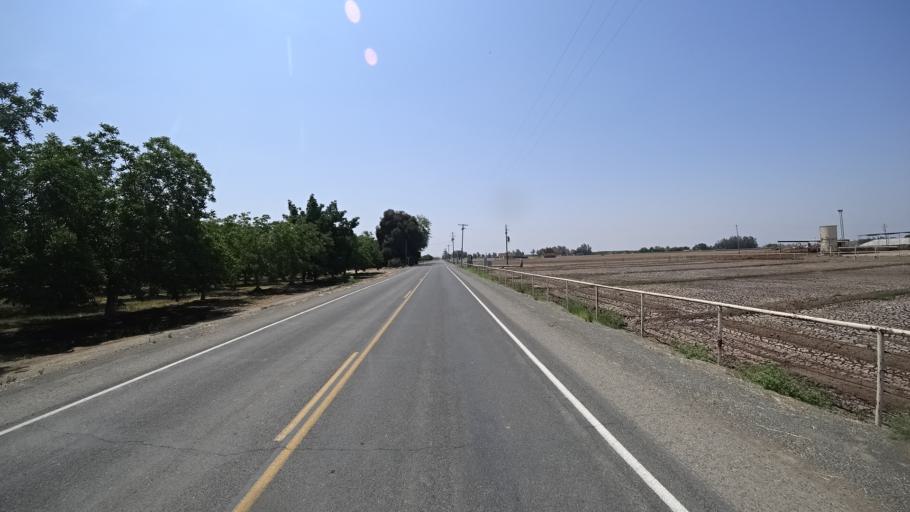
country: US
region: California
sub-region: Kings County
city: Lemoore
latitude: 36.3507
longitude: -119.7809
